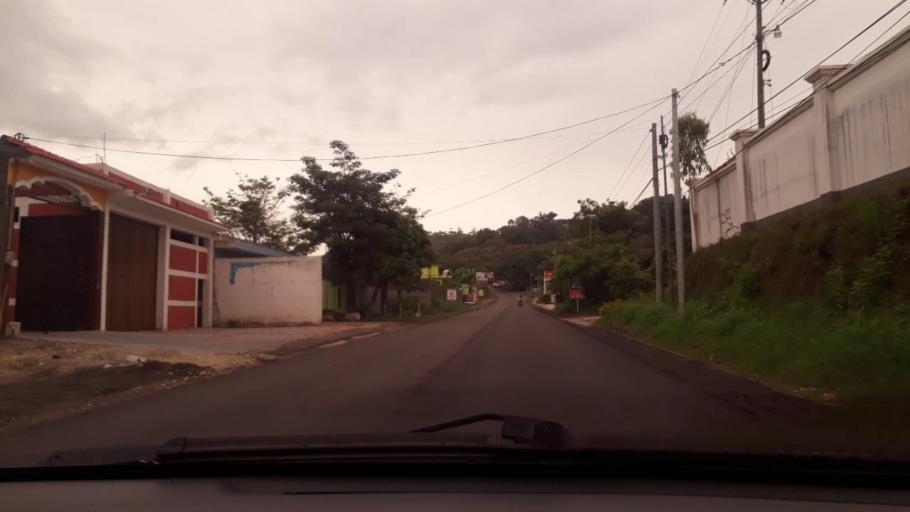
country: GT
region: Chiquimula
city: Concepcion Las Minas
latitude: 14.5404
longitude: -89.4632
